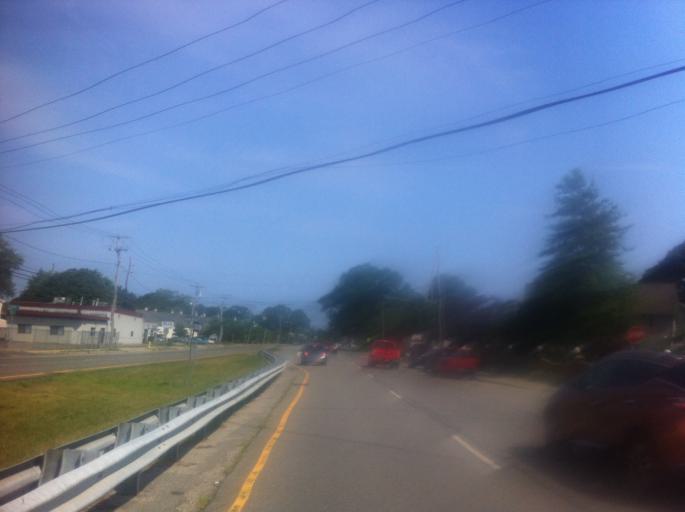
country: US
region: New York
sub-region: Suffolk County
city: West Babylon
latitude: 40.7072
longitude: -73.3512
